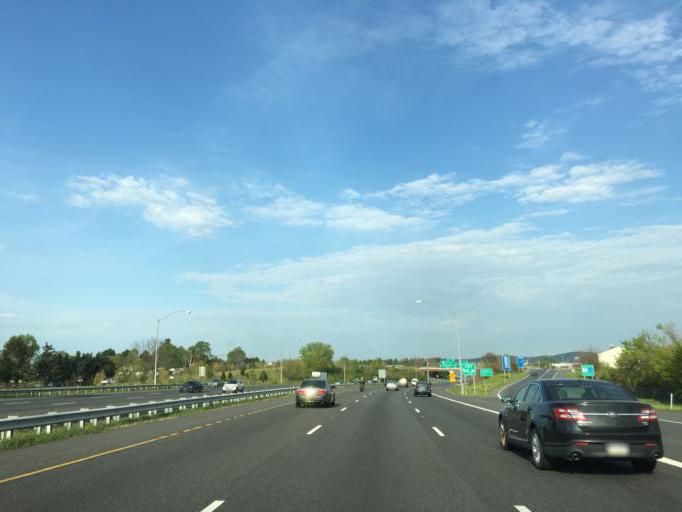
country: US
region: Maryland
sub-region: Frederick County
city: Bartonsville
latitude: 39.4039
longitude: -77.3781
